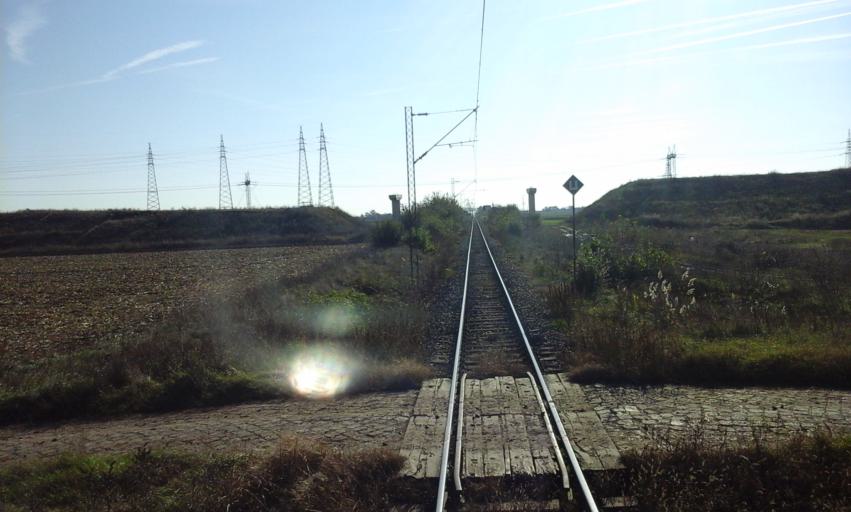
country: RS
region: Autonomna Pokrajina Vojvodina
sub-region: Severnobacki Okrug
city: Subotica
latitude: 46.0354
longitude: 19.6830
